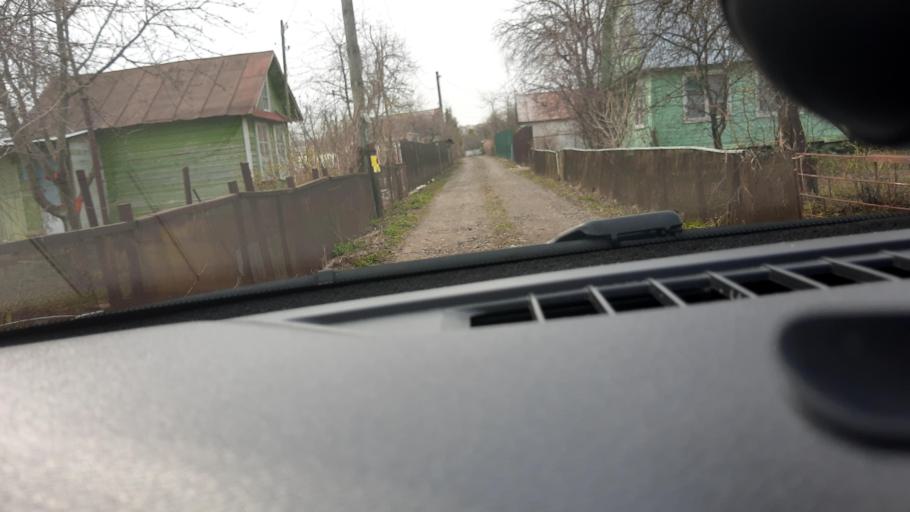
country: RU
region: Nizjnij Novgorod
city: Gorbatovka
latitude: 56.3858
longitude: 43.8215
